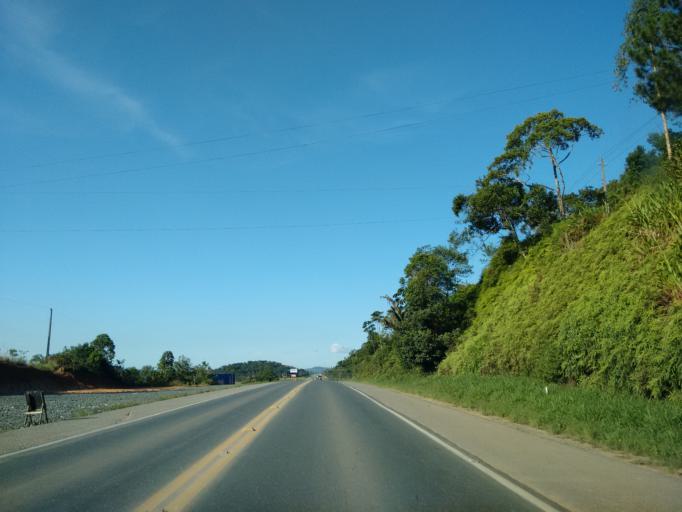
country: BR
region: Santa Catarina
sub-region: Guaramirim
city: Guaramirim
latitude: -26.4532
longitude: -48.9128
